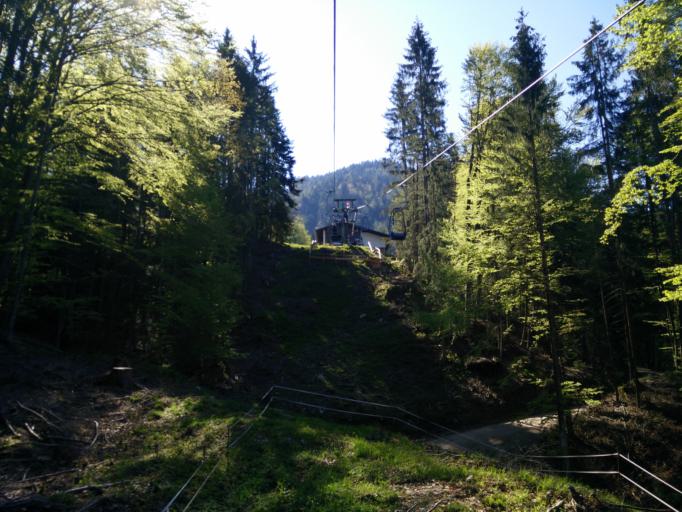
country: DE
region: Bavaria
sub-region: Upper Bavaria
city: Kiefersfelden
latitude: 47.5840
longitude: 12.1980
